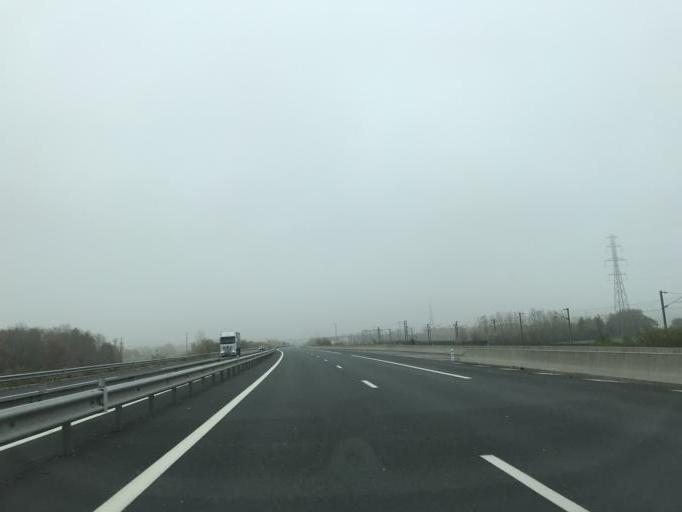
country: FR
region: Rhone-Alpes
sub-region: Departement de l'Ain
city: Tramoyes
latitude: 45.8586
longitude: 4.9488
